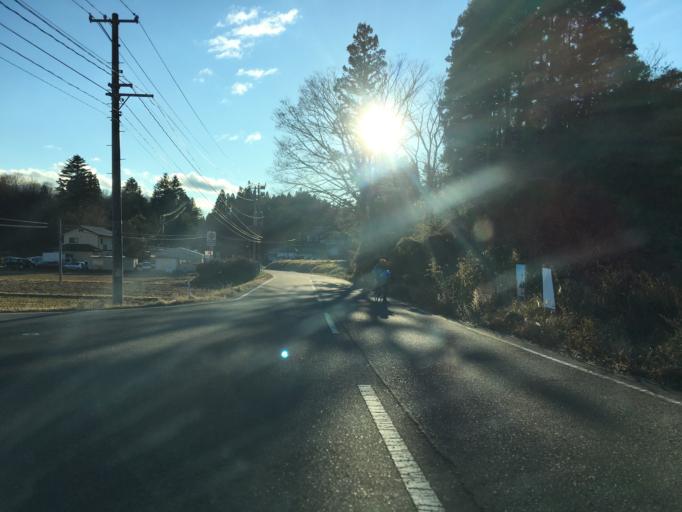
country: JP
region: Fukushima
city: Ishikawa
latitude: 37.1771
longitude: 140.5459
